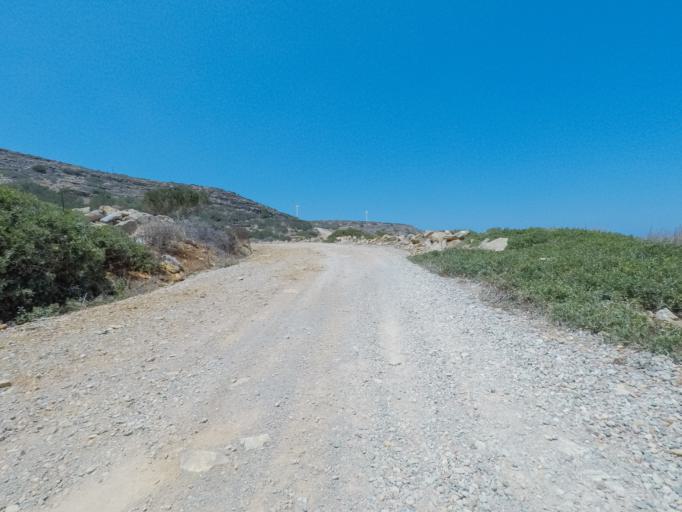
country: GR
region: Crete
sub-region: Nomos Lasithiou
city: Elounda
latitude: 35.3248
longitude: 25.7614
